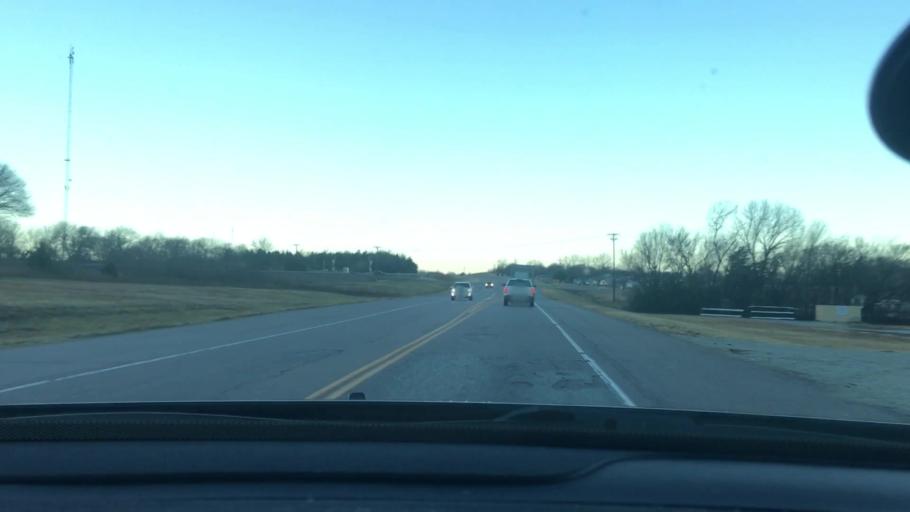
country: US
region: Oklahoma
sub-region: Pontotoc County
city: Ada
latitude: 34.7483
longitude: -96.7034
